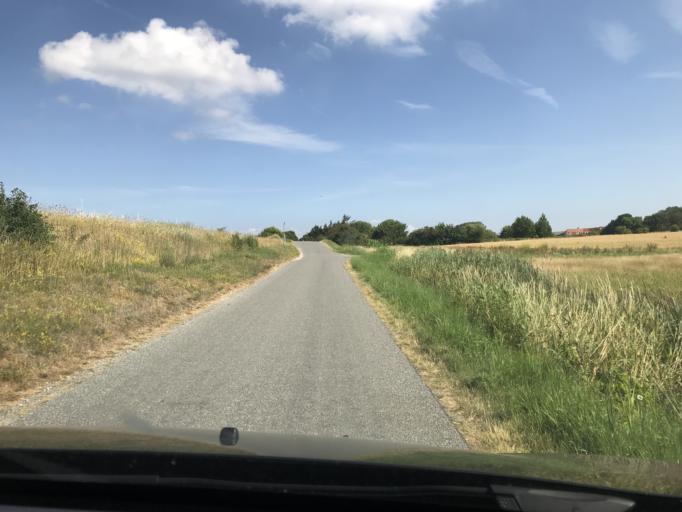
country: DK
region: South Denmark
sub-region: AEro Kommune
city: AEroskobing
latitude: 54.8848
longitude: 10.3826
